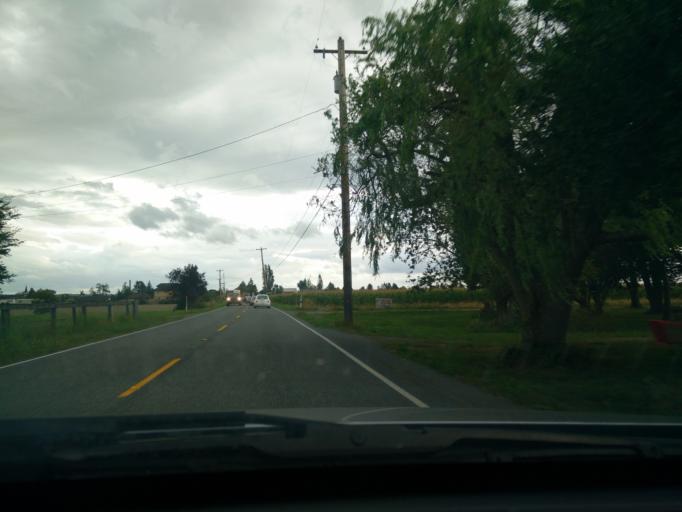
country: US
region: Washington
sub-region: Snohomish County
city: Stanwood
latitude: 48.2508
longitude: -122.3710
